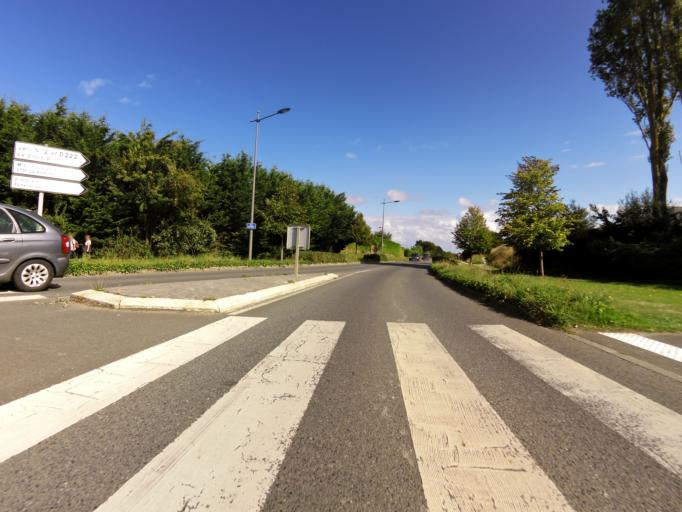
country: FR
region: Brittany
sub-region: Departement des Cotes-d'Armor
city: Langueux
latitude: 48.4849
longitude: -2.7400
